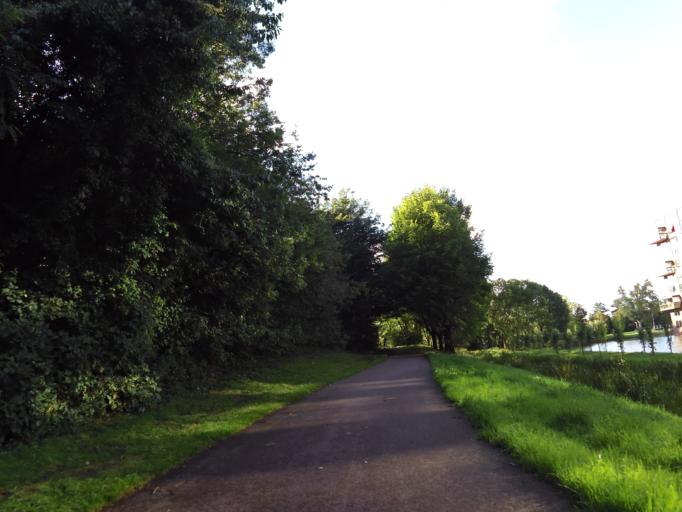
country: NL
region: South Holland
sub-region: Gemeente Leiden
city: Leiden
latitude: 52.1463
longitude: 4.5097
